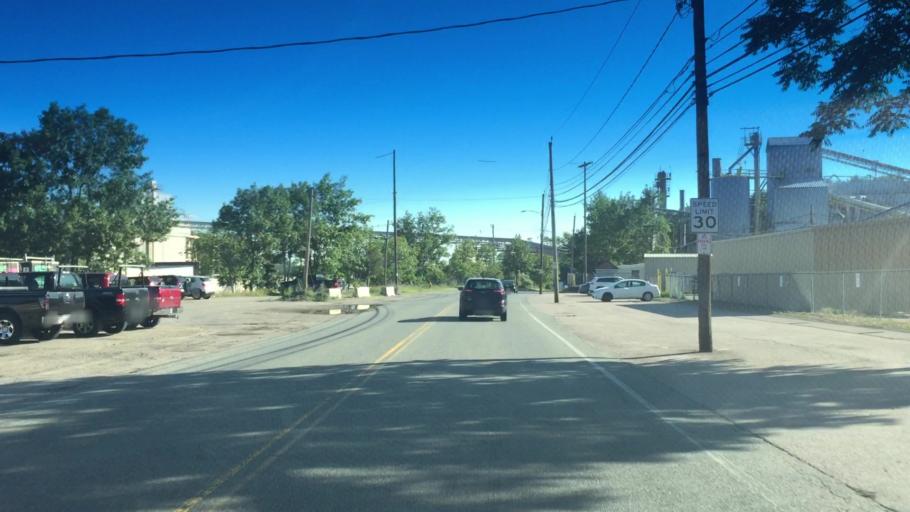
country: US
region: Massachusetts
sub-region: Norfolk County
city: Norwood
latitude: 42.1656
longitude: -71.2075
